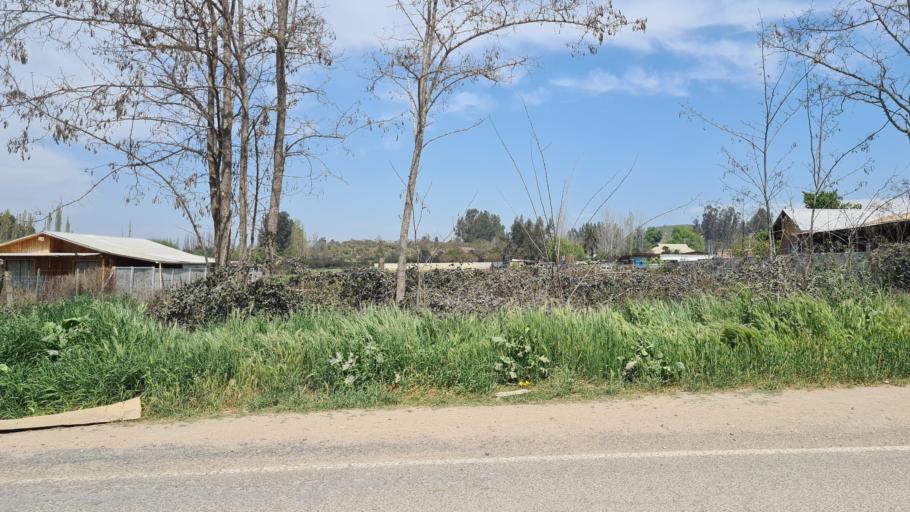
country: CL
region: O'Higgins
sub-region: Provincia de Cachapoal
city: San Vicente
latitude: -34.1781
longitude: -71.4044
